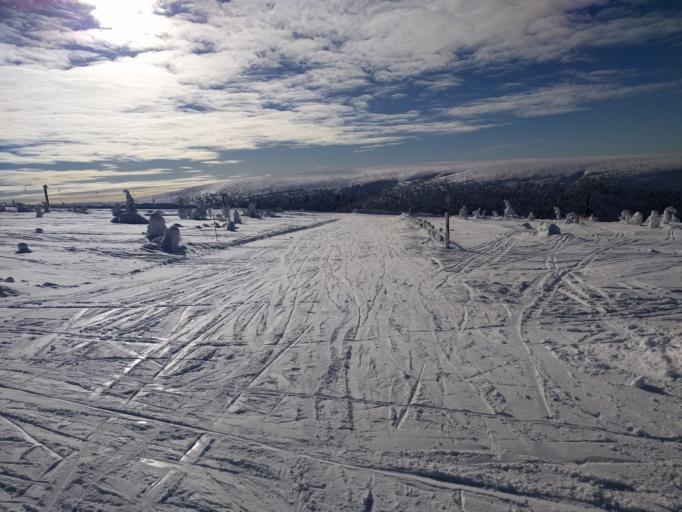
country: NO
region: Hedmark
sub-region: Trysil
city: Innbygda
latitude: 61.1738
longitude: 13.0166
